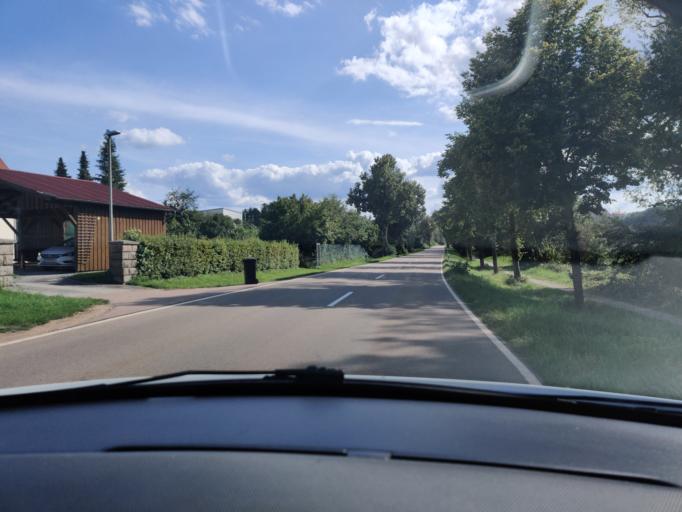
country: DE
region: Bavaria
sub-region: Upper Palatinate
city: Nabburg
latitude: 49.4643
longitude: 12.1865
